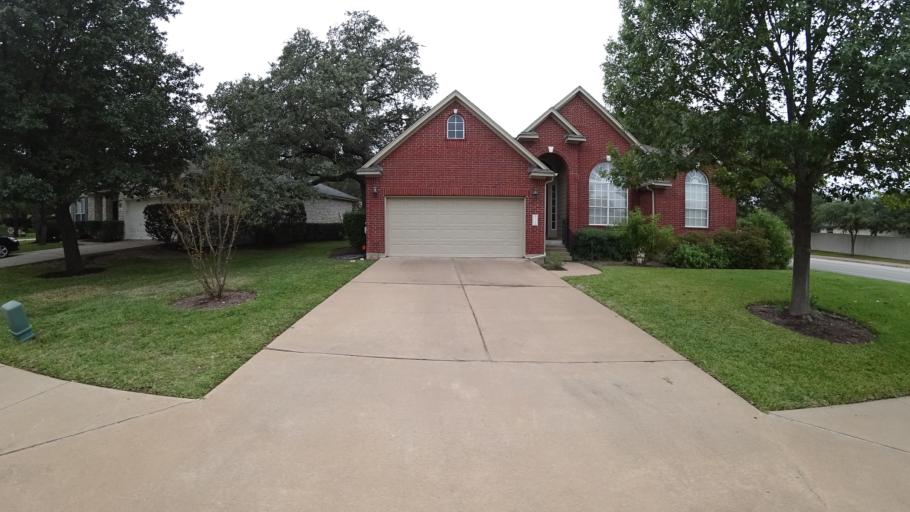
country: US
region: Texas
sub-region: Travis County
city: Bee Cave
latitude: 30.3095
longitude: -97.9253
